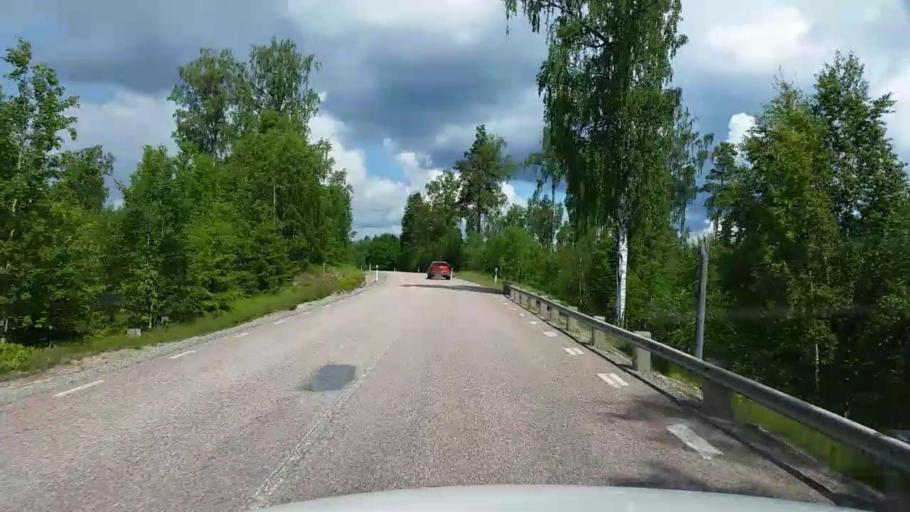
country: SE
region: Vaestmanland
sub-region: Skinnskattebergs Kommun
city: Skinnskatteberg
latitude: 59.7856
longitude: 15.8597
